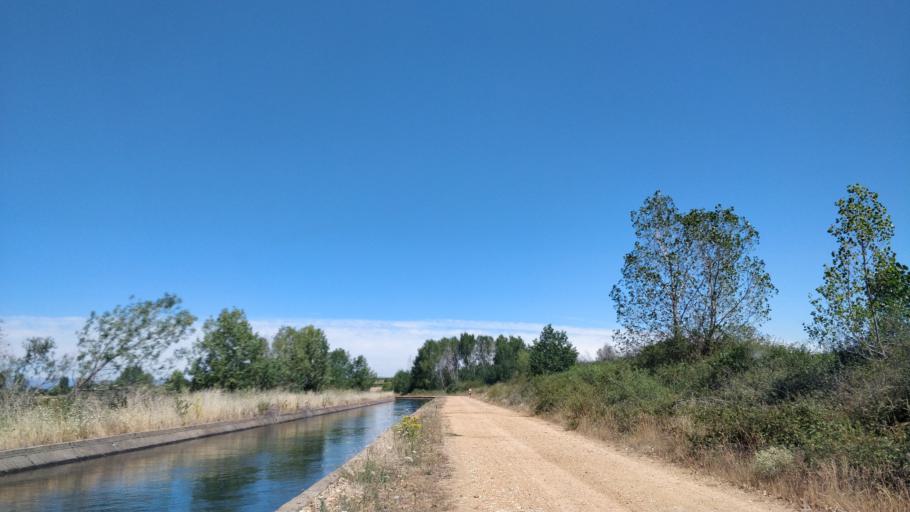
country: ES
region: Castille and Leon
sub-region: Provincia de Leon
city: Bustillo del Paramo
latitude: 42.4766
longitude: -5.8055
